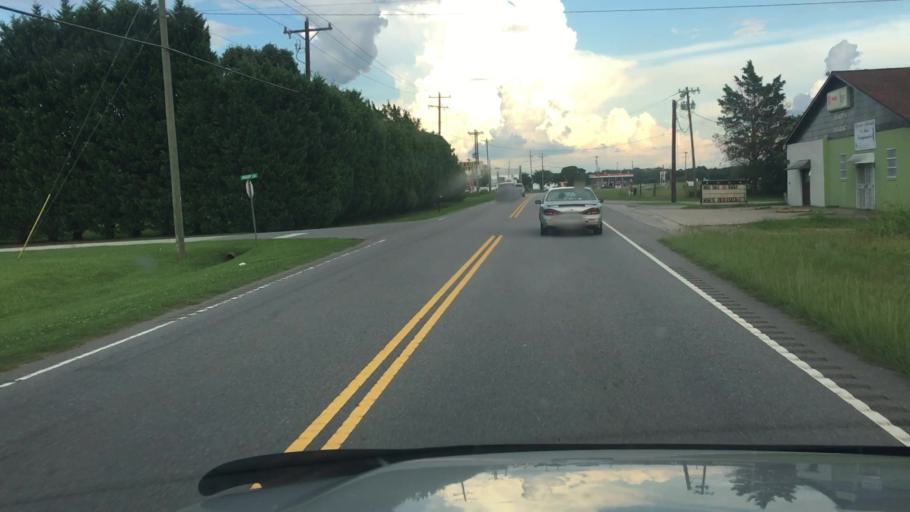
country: US
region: South Carolina
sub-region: Cherokee County
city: Gaffney
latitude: 35.1135
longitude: -81.7035
